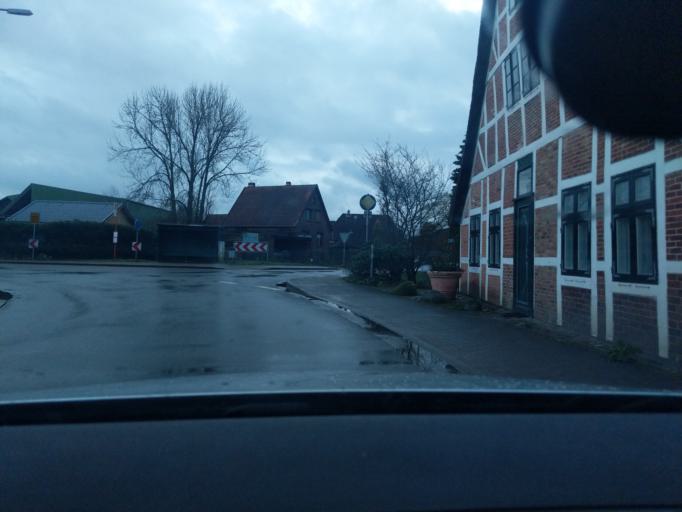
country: DE
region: Lower Saxony
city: Mittelnkirchen
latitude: 53.5250
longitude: 9.6452
